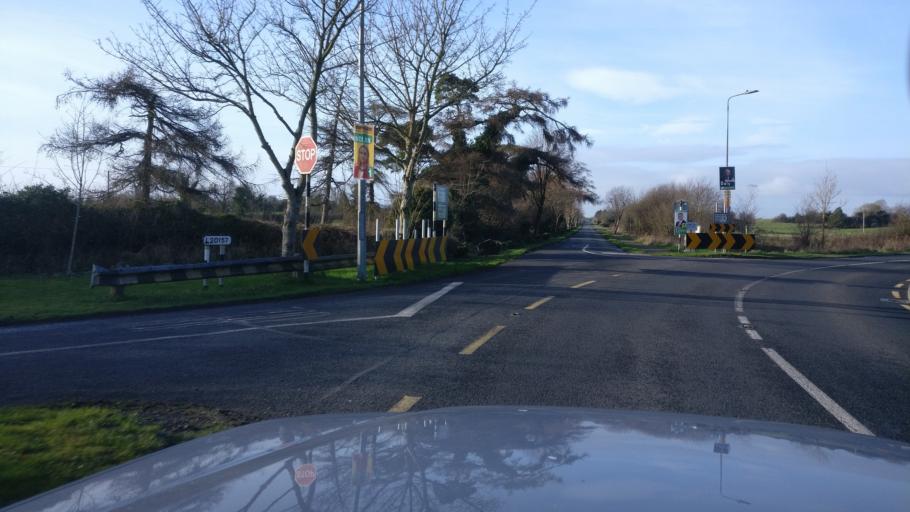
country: IE
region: Leinster
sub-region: Uibh Fhaili
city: Clara
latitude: 53.3477
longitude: -7.6216
